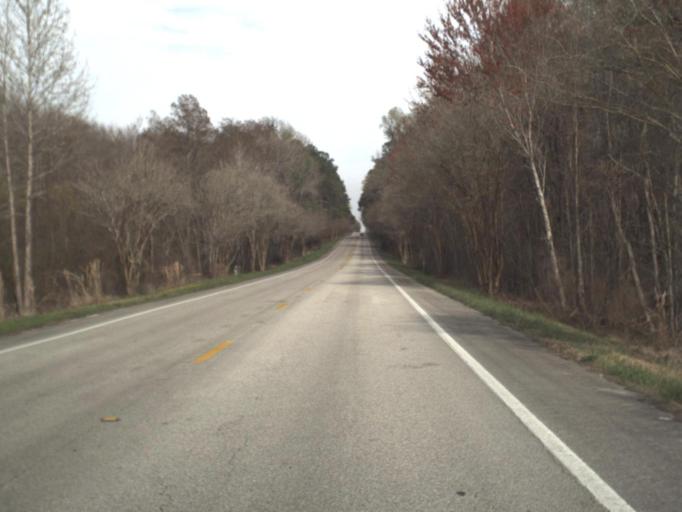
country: US
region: Florida
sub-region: Jefferson County
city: Monticello
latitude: 30.5298
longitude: -83.9682
